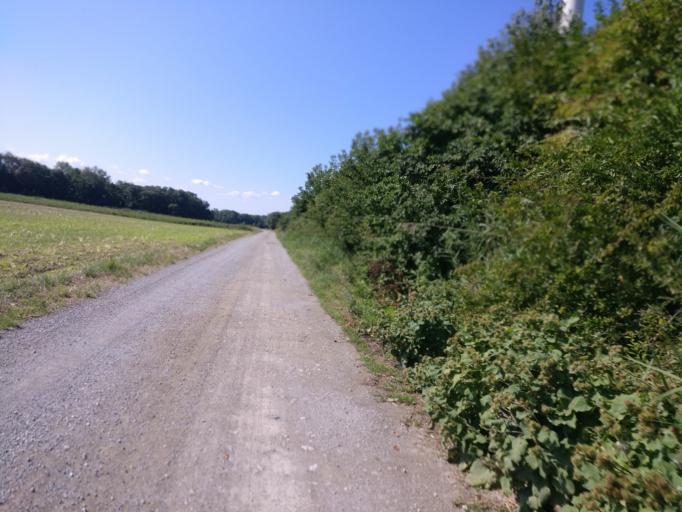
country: AT
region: Lower Austria
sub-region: Politischer Bezirk Baden
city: Ebreichsdorf
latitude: 47.9330
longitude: 16.3717
